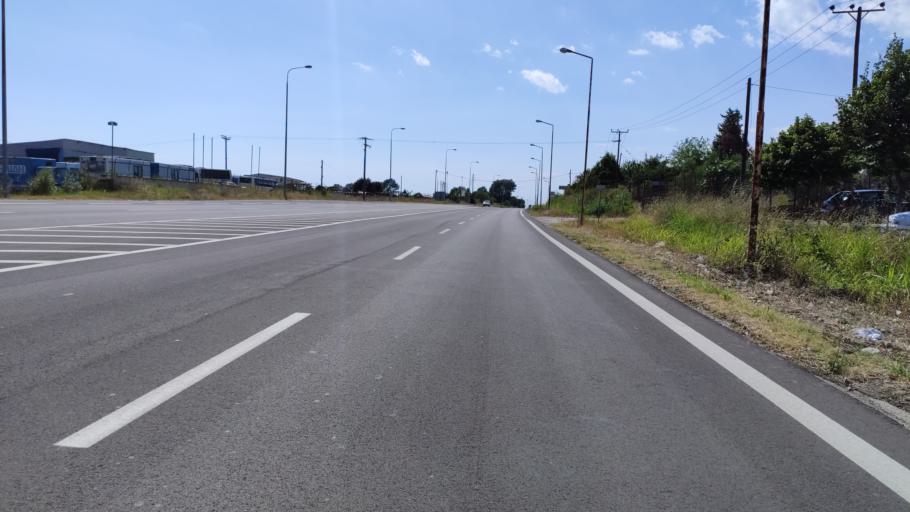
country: GR
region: East Macedonia and Thrace
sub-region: Nomos Rodopis
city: Komotini
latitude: 41.1086
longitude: 25.3577
